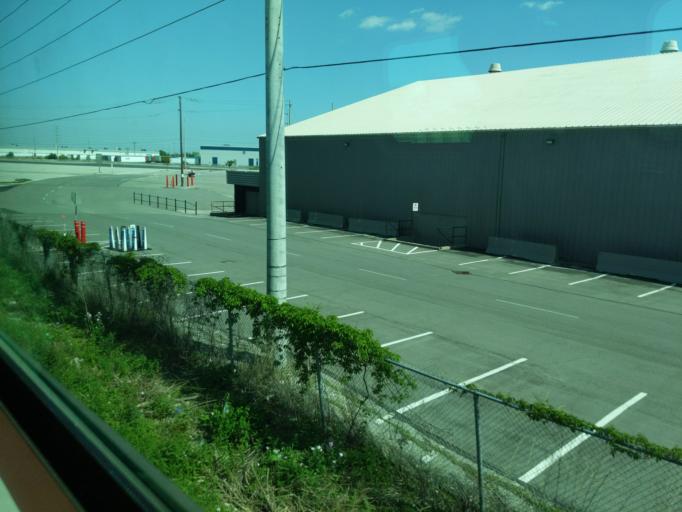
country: CA
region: Ontario
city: Etobicoke
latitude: 43.7049
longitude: -79.6358
